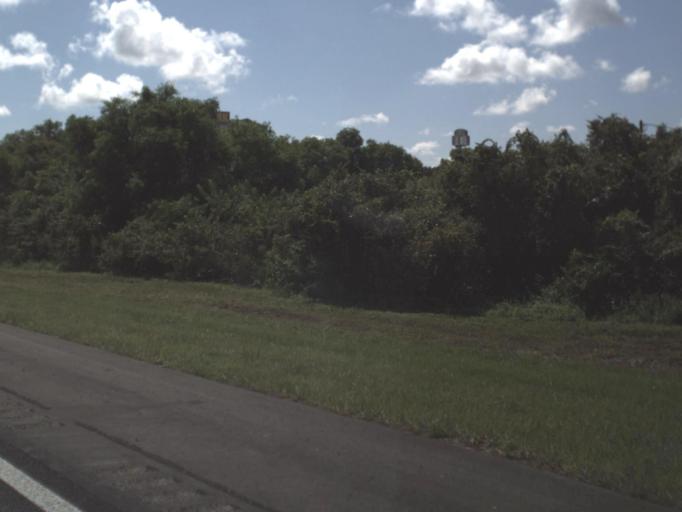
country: US
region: Florida
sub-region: Lee County
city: Suncoast Estates
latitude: 26.7230
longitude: -81.8261
